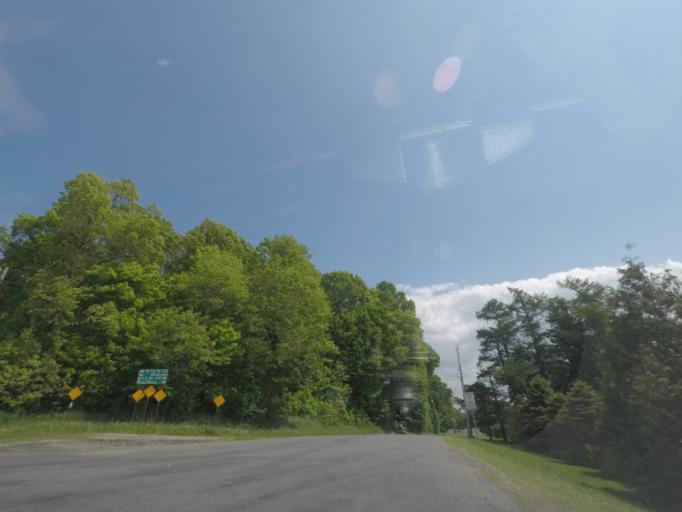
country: US
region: New York
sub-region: Dutchess County
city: Pine Plains
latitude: 41.9810
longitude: -73.5511
